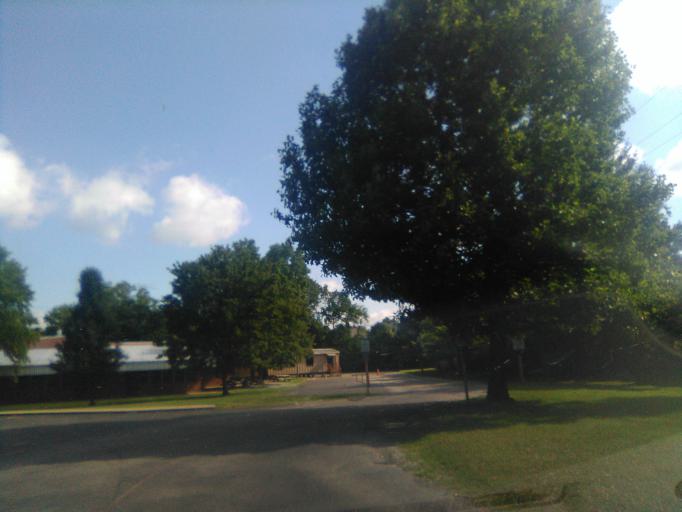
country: US
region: Tennessee
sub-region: Davidson County
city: Belle Meade
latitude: 36.1160
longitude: -86.8658
